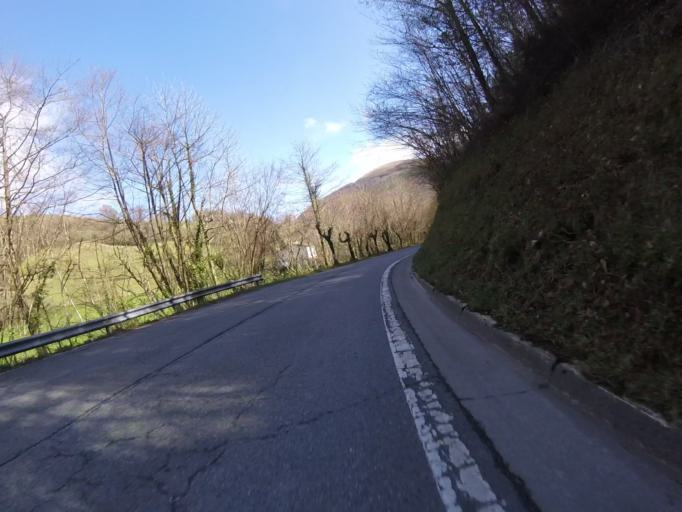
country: ES
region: Navarre
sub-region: Provincia de Navarra
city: Leitza
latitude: 43.0881
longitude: -1.8708
